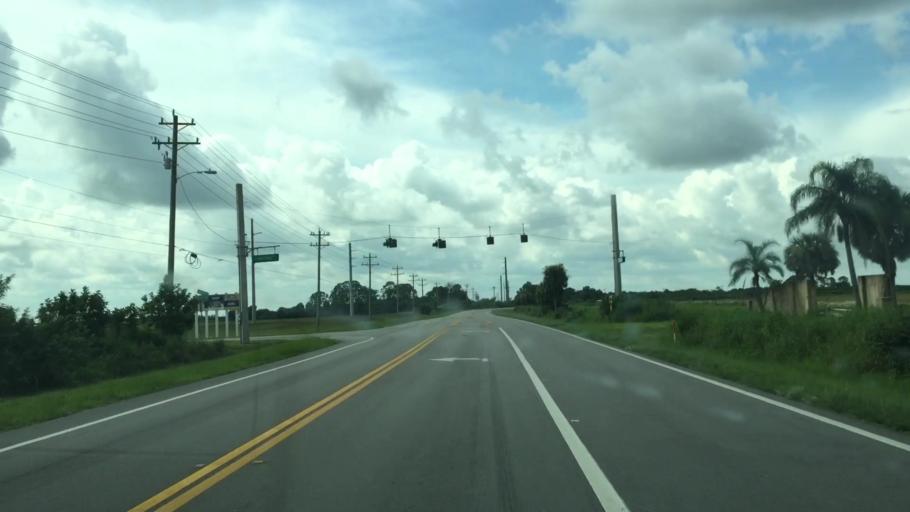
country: US
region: Florida
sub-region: Collier County
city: Immokalee
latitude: 26.3756
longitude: -81.4171
